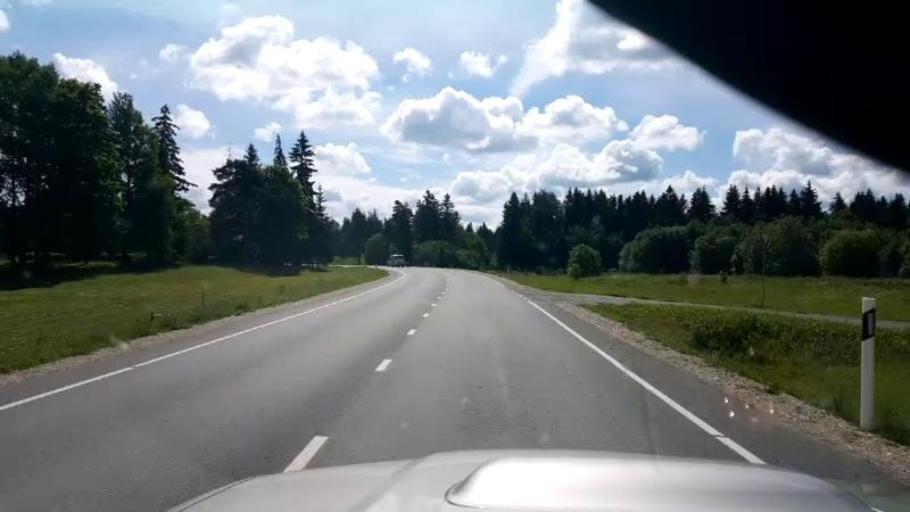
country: EE
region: Laeaene-Virumaa
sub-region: Tapa vald
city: Tapa
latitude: 59.2560
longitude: 25.9620
